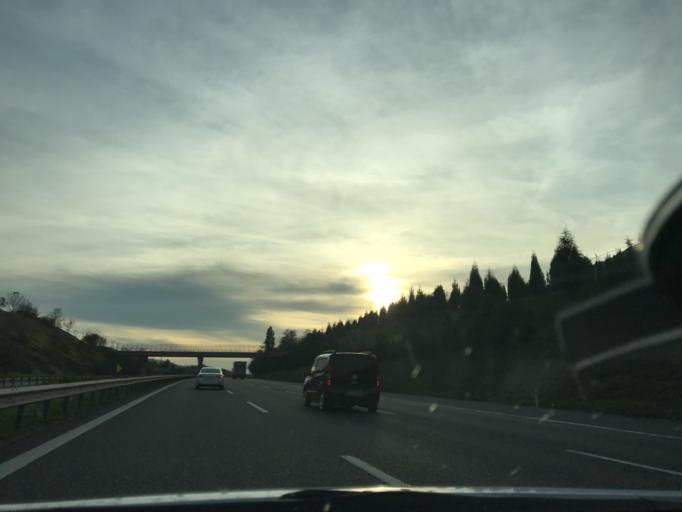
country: TR
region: Duzce
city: Gumusova
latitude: 40.8189
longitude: 30.9143
